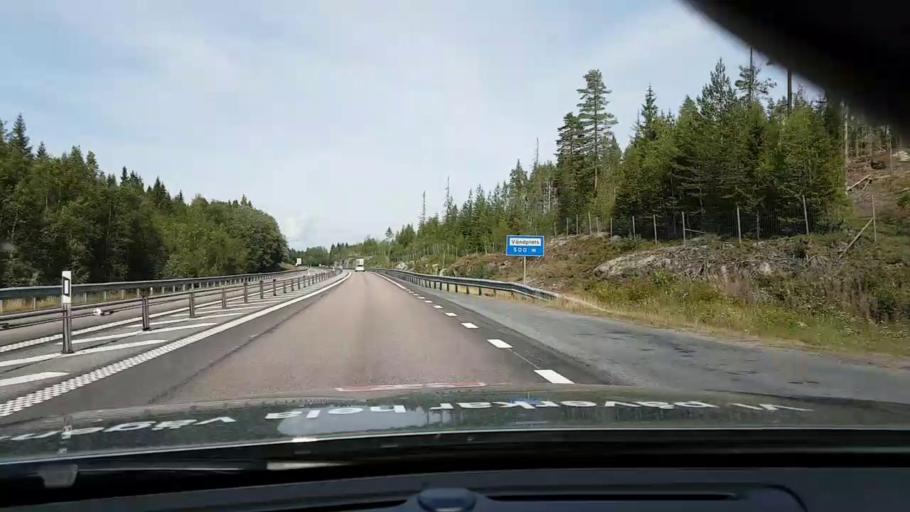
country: SE
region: Vaesternorrland
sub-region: OErnskoeldsviks Kommun
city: Husum
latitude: 63.4313
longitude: 19.2096
